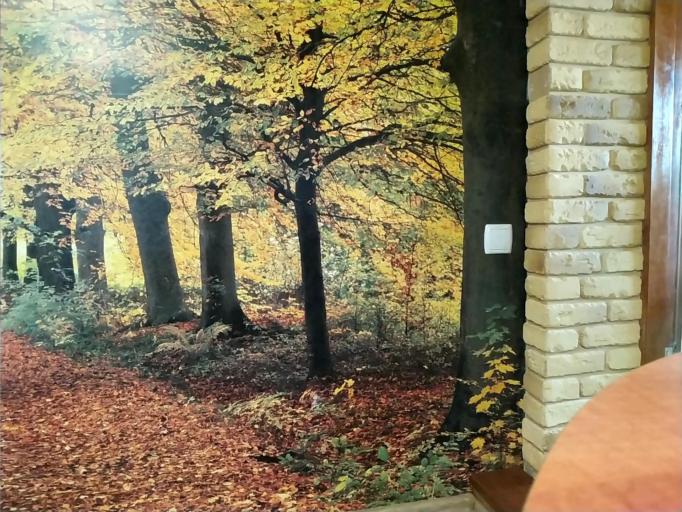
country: RU
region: Leningrad
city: Tolmachevo
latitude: 58.9429
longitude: 29.6645
